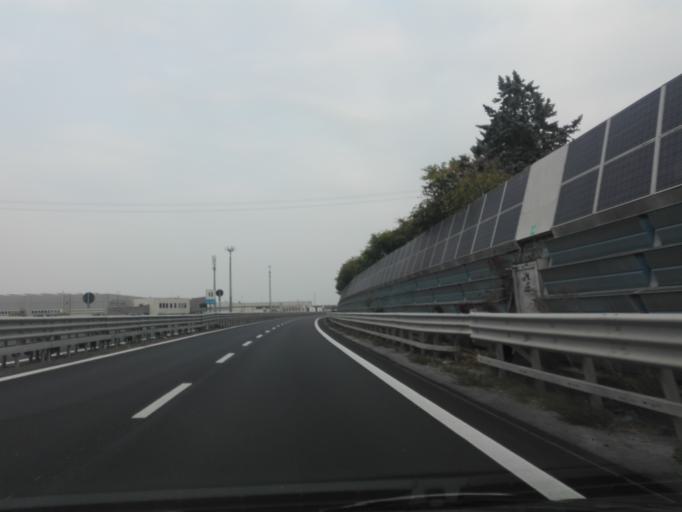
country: IT
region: Veneto
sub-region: Provincia di Verona
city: Vallese
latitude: 45.3282
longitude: 11.0810
